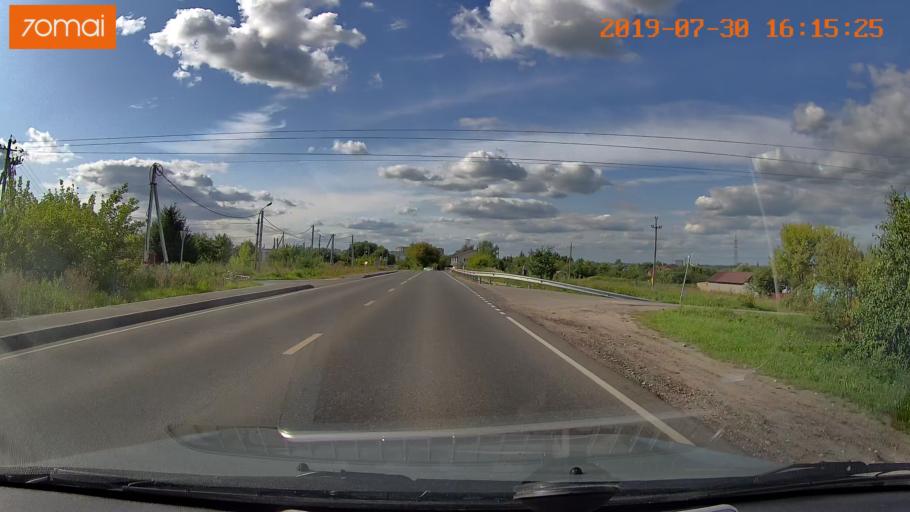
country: RU
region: Moskovskaya
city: Voskresensk
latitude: 55.2960
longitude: 38.6677
